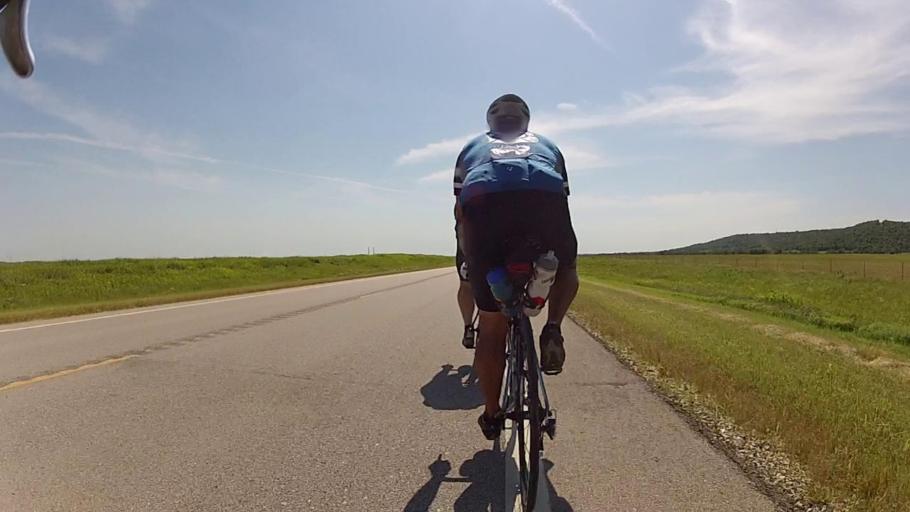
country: US
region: Kansas
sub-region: Chautauqua County
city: Sedan
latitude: 37.1068
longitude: -96.5570
